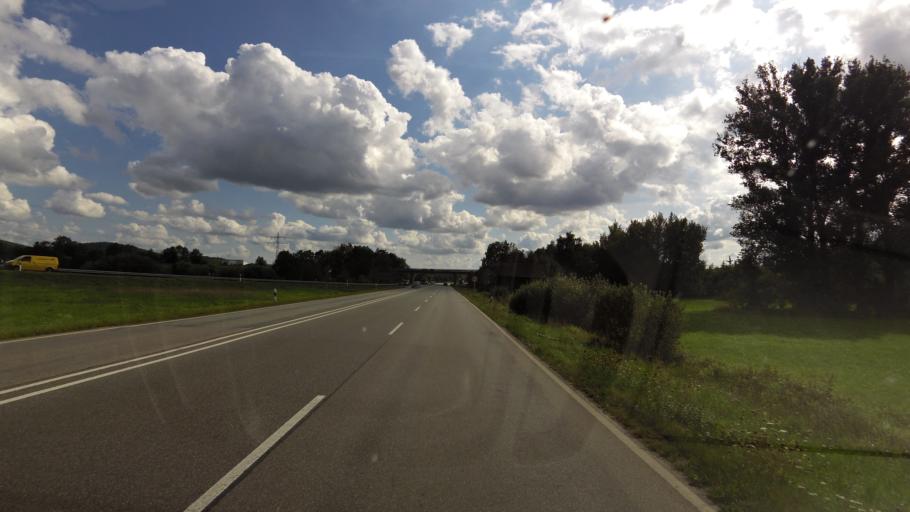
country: DE
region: Bavaria
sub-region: Upper Palatinate
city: Cham
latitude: 49.2129
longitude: 12.6784
